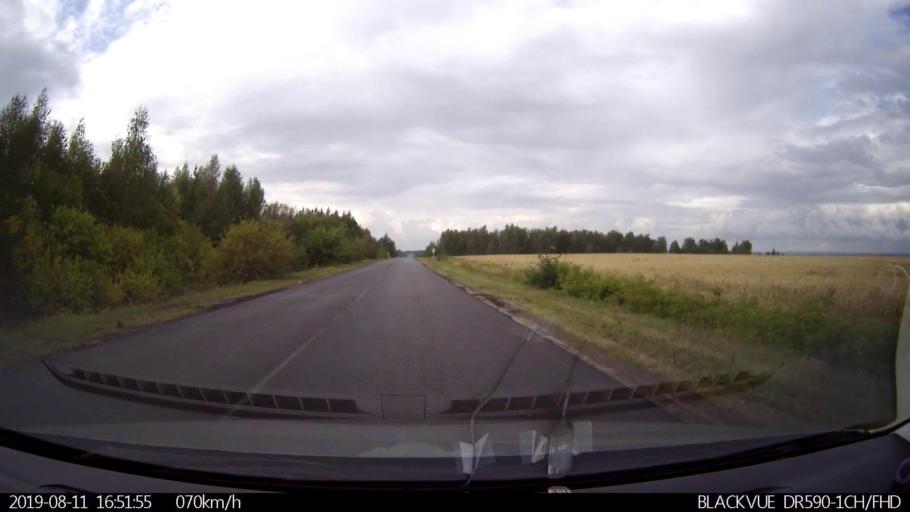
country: RU
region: Ulyanovsk
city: Mayna
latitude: 54.2422
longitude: 47.6756
